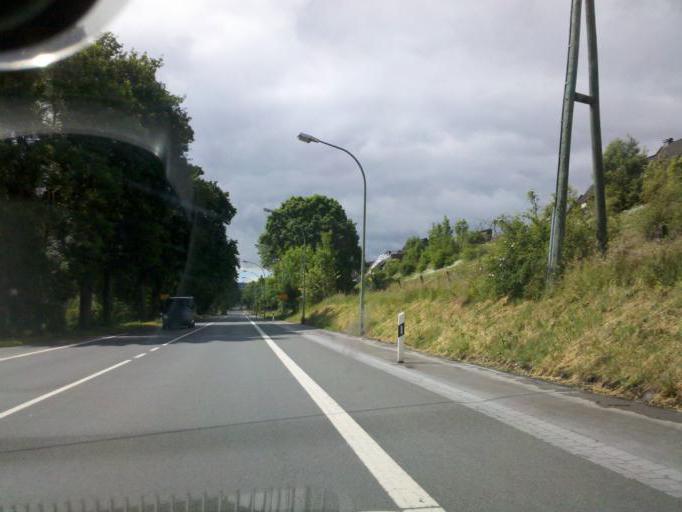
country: DE
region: North Rhine-Westphalia
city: Warstein
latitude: 51.4342
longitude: 8.3475
